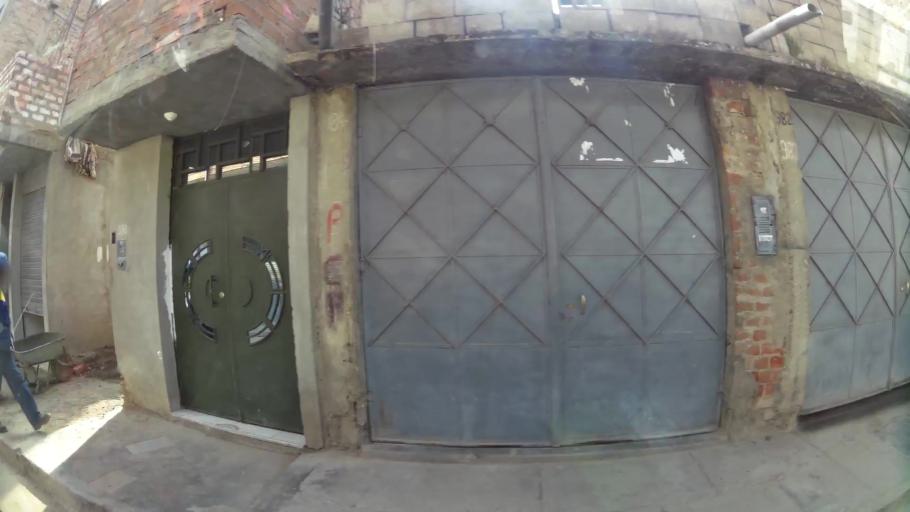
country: PE
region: Junin
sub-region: Provincia de Huancayo
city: El Tambo
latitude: -12.0738
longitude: -75.2124
